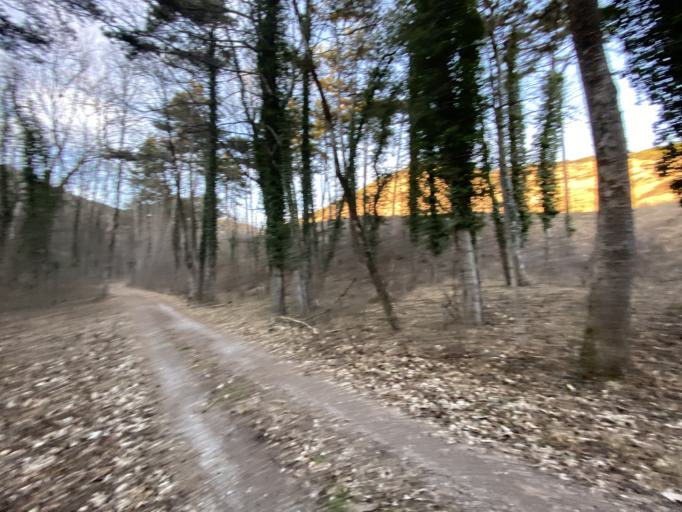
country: AT
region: Lower Austria
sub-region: Politischer Bezirk Baden
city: Hirtenberg
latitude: 47.9750
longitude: 16.1545
